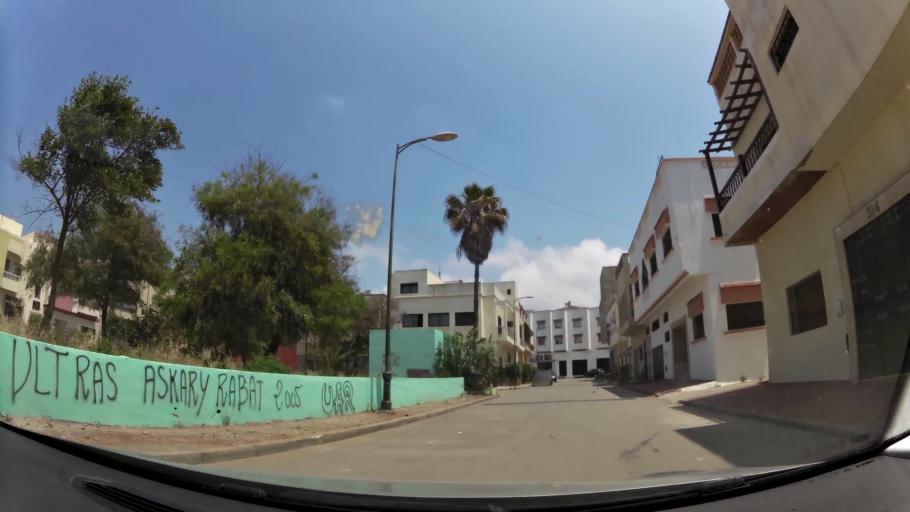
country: MA
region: Rabat-Sale-Zemmour-Zaer
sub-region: Skhirate-Temara
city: Temara
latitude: 33.9786
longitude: -6.8955
